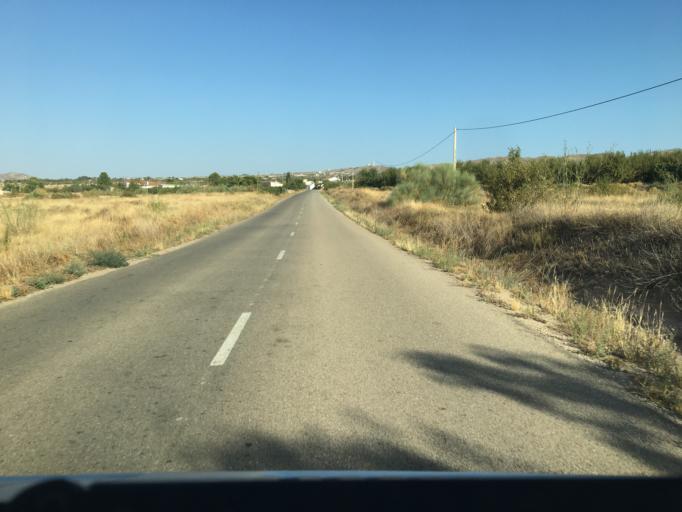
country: ES
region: Andalusia
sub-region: Provincia de Almeria
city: Huercal-Overa
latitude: 37.4677
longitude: -1.8883
